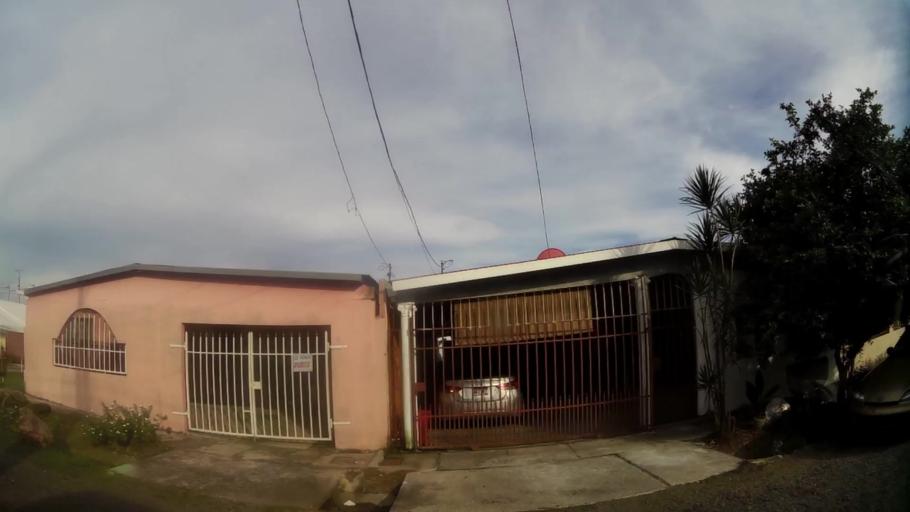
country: PA
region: Panama
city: La Chorrera
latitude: 8.8967
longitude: -79.7647
